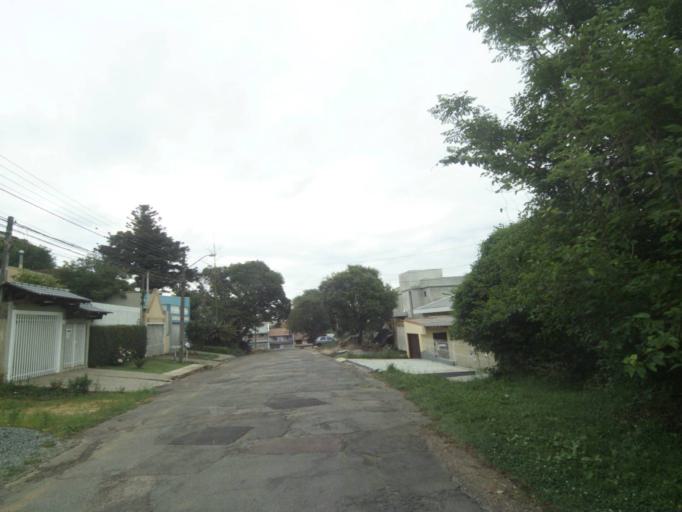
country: BR
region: Parana
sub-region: Curitiba
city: Curitiba
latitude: -25.3927
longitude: -49.2927
